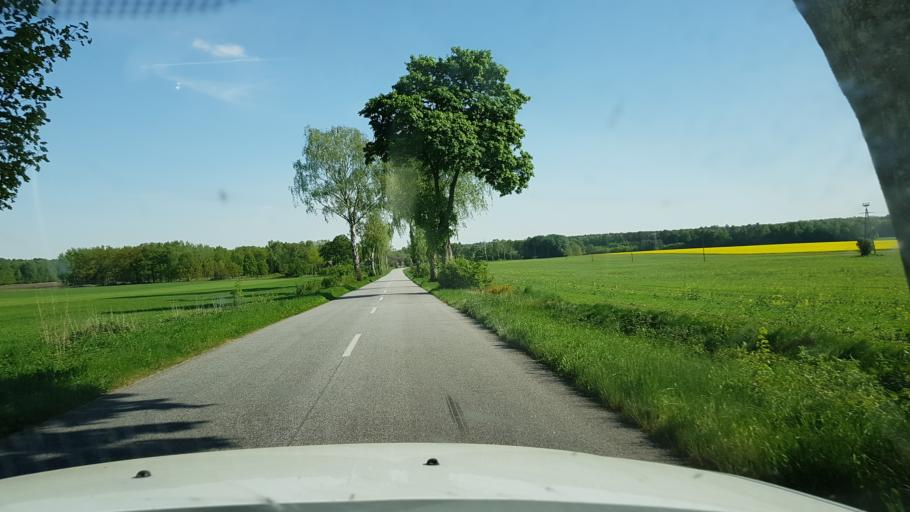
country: PL
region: West Pomeranian Voivodeship
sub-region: Powiat lobeski
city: Resko
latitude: 53.8264
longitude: 15.3919
